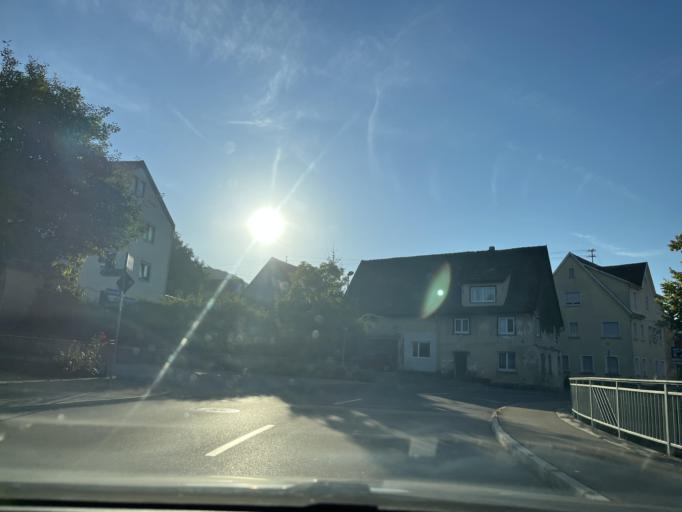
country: DE
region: Baden-Wuerttemberg
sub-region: Tuebingen Region
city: Jungingen
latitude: 48.3271
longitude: 9.0415
